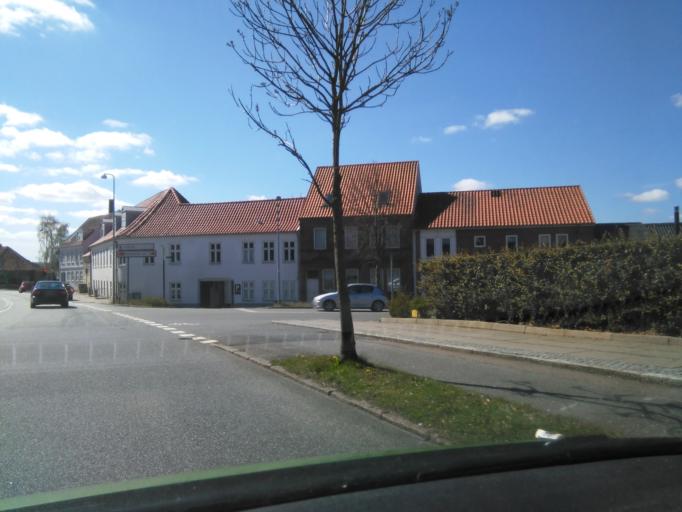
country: DK
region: Central Jutland
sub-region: Horsens Kommune
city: Horsens
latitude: 55.8705
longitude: 9.8442
